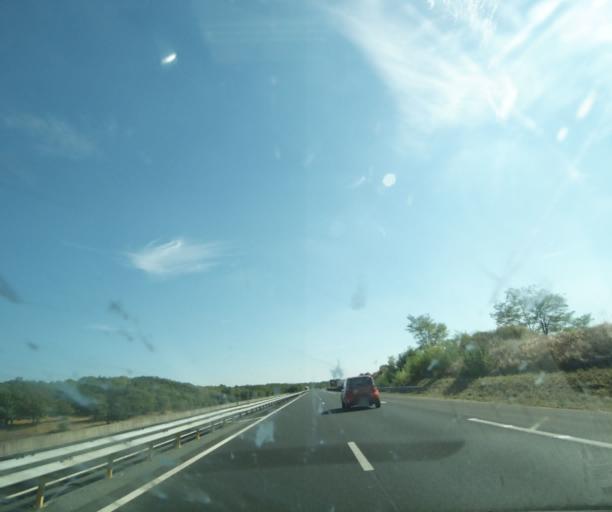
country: FR
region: Limousin
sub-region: Departement de la Correze
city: Cosnac
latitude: 45.0261
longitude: 1.5308
